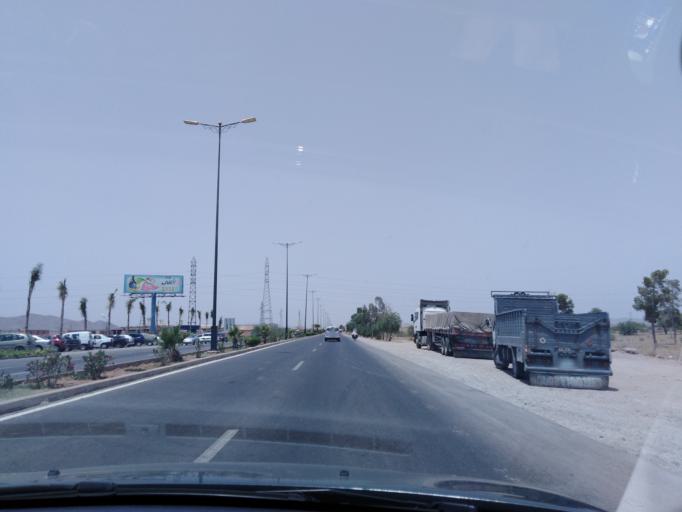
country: MA
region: Marrakech-Tensift-Al Haouz
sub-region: Marrakech
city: Marrakesh
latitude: 31.7211
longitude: -7.9815
